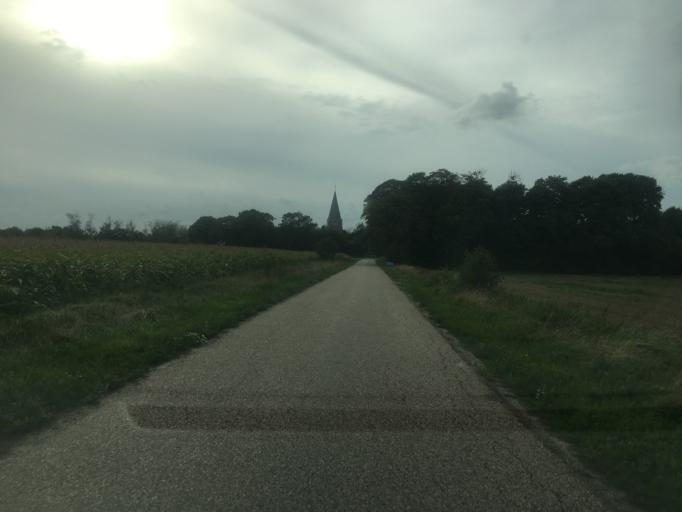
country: DE
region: Schleswig-Holstein
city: Aventoft
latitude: 54.9696
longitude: 8.7501
